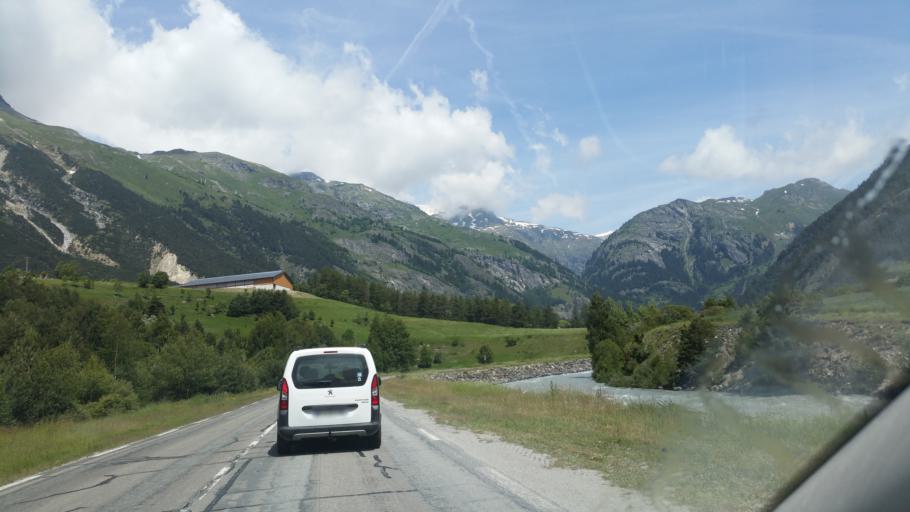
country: FR
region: Rhone-Alpes
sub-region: Departement de la Savoie
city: Modane
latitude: 45.2695
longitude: 6.8143
